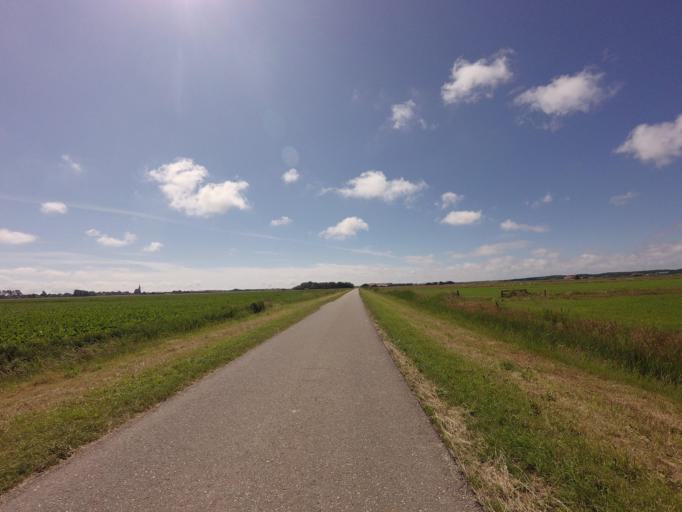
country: NL
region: North Holland
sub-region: Gemeente Texel
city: Den Burg
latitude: 53.0343
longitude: 4.7633
